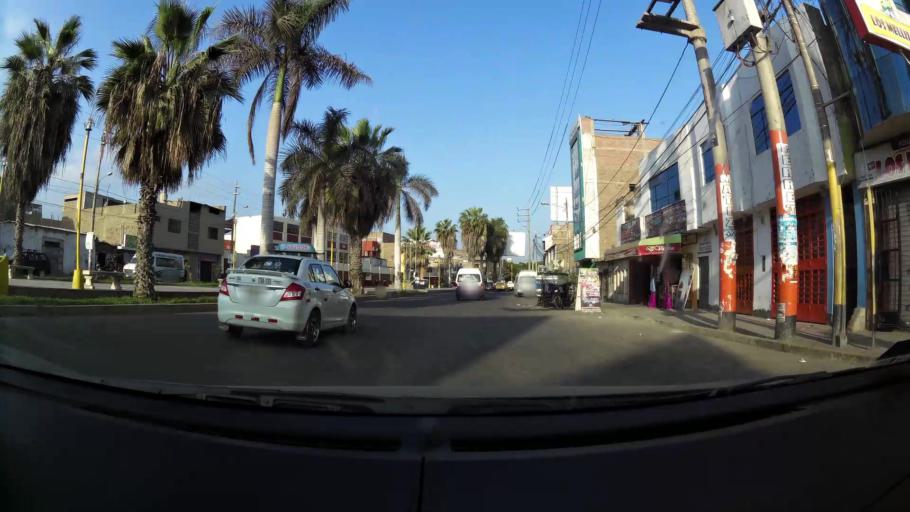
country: PE
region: La Libertad
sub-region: Provincia de Trujillo
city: El Porvenir
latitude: -8.0868
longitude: -79.0031
